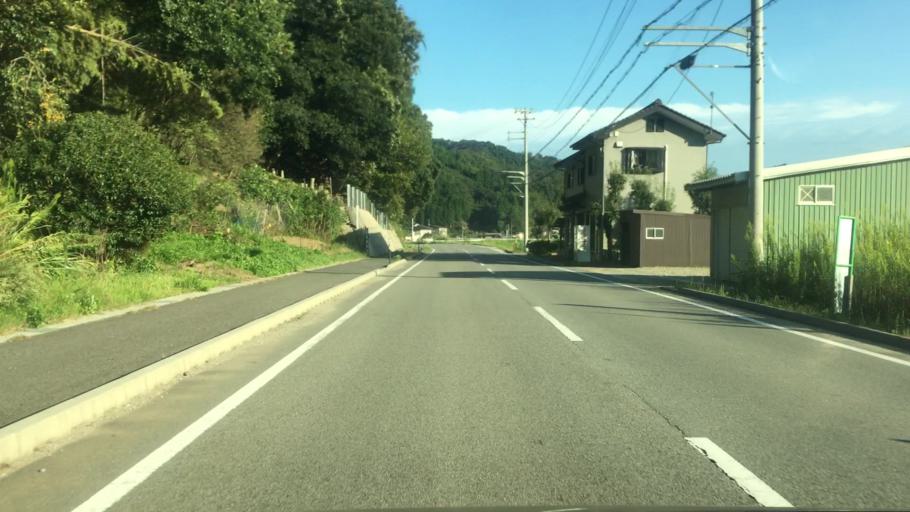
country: JP
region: Hyogo
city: Toyooka
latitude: 35.5864
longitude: 134.8057
